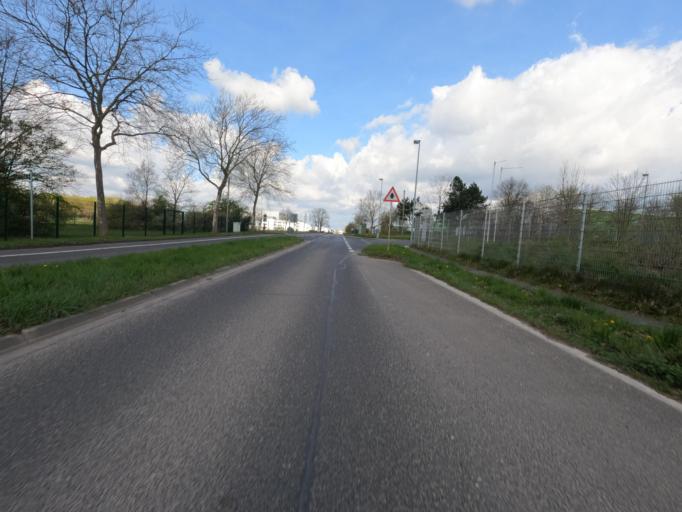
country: DE
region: North Rhine-Westphalia
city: Huckelhoven
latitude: 51.0310
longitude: 6.2604
